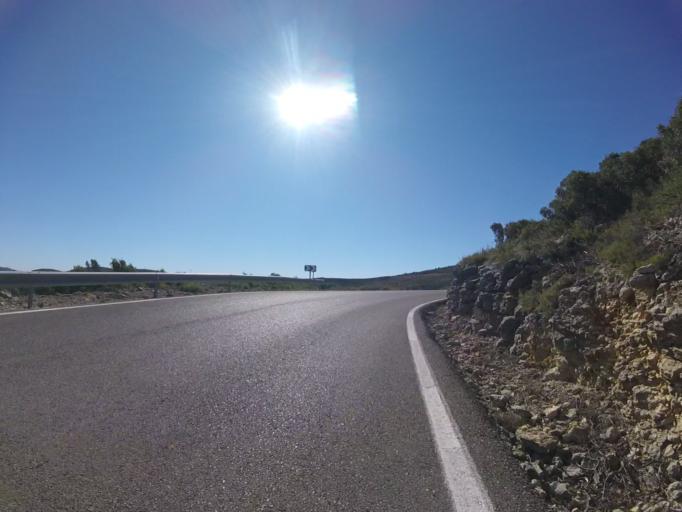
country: ES
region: Valencia
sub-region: Provincia de Castello
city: Albocasser
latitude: 40.3928
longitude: 0.0404
